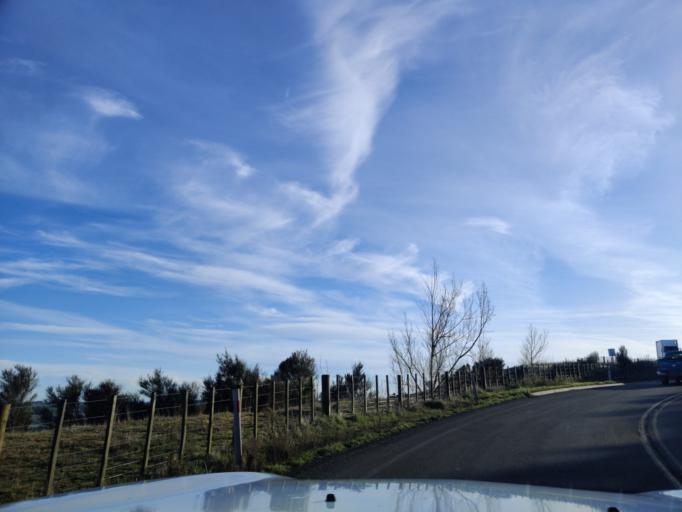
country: NZ
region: Manawatu-Wanganui
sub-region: Palmerston North City
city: Palmerston North
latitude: -40.2877
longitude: 175.7864
